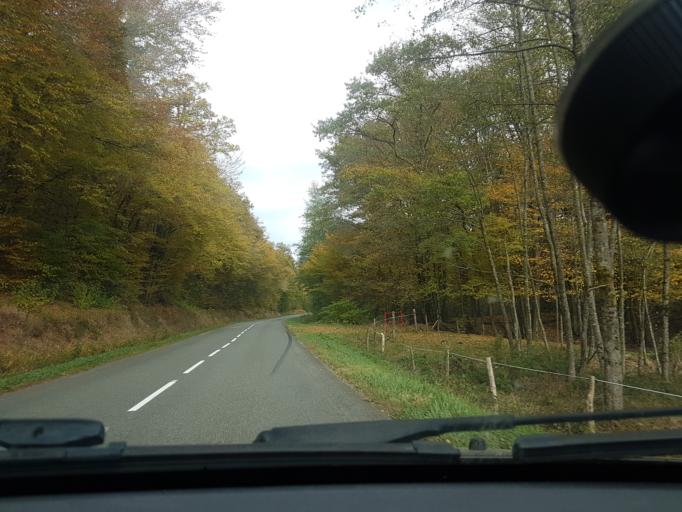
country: FR
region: Franche-Comte
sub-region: Departement de la Haute-Saone
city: Frahier-et-Chatebier
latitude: 47.6718
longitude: 6.7381
